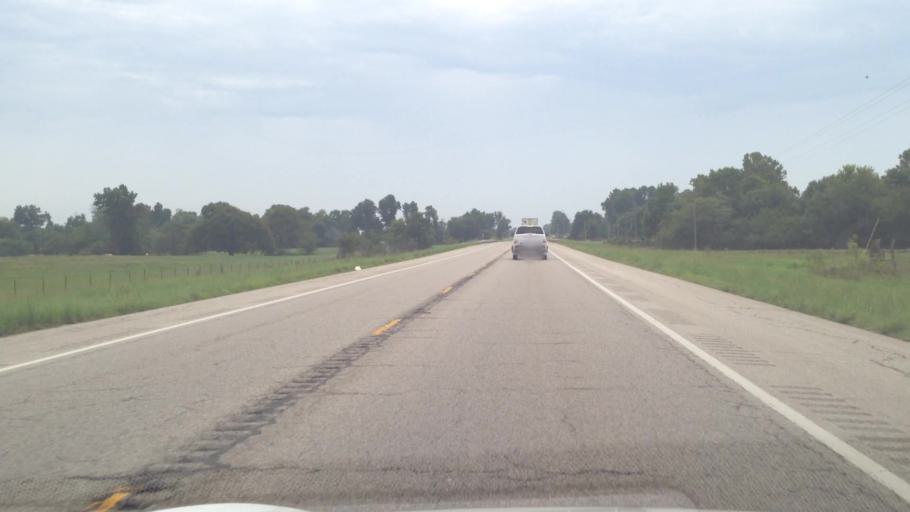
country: US
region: Missouri
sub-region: Jasper County
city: Carl Junction
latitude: 37.2042
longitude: -94.7047
